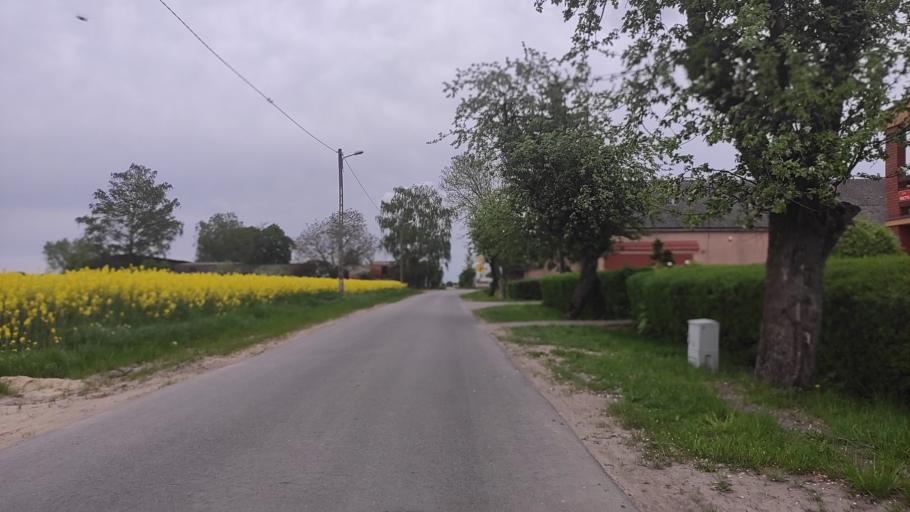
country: PL
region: Greater Poland Voivodeship
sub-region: Powiat poznanski
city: Swarzedz
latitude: 52.4117
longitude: 17.1262
